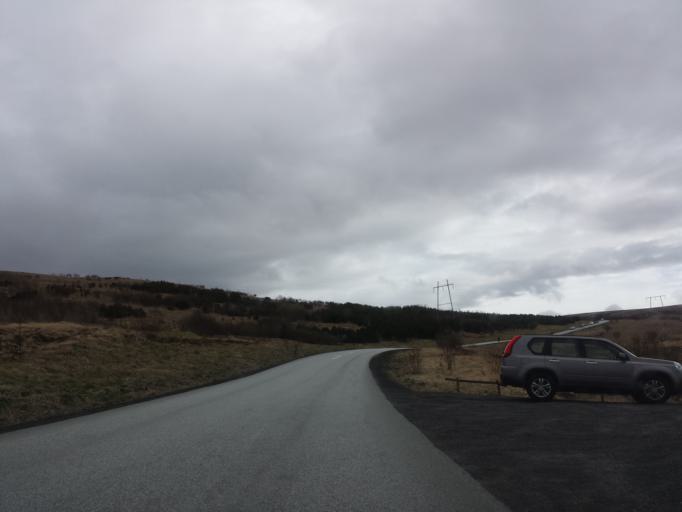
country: IS
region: Capital Region
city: Kopavogur
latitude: 64.0824
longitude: -21.8684
